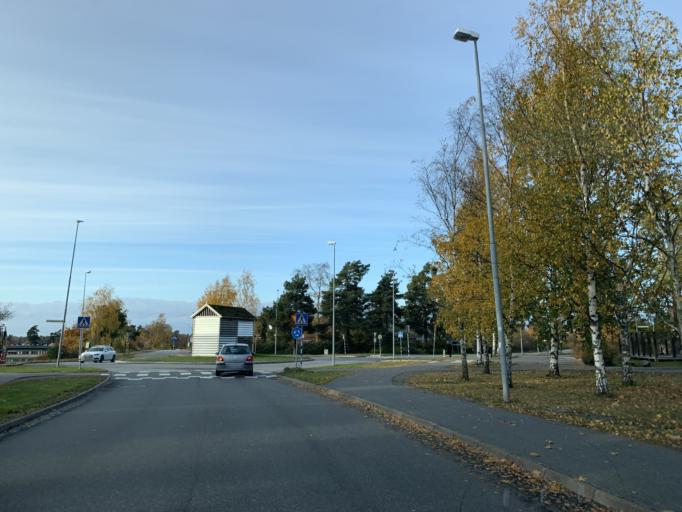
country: SE
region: Stockholm
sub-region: Haninge Kommun
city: Haninge
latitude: 59.1802
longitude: 18.1810
